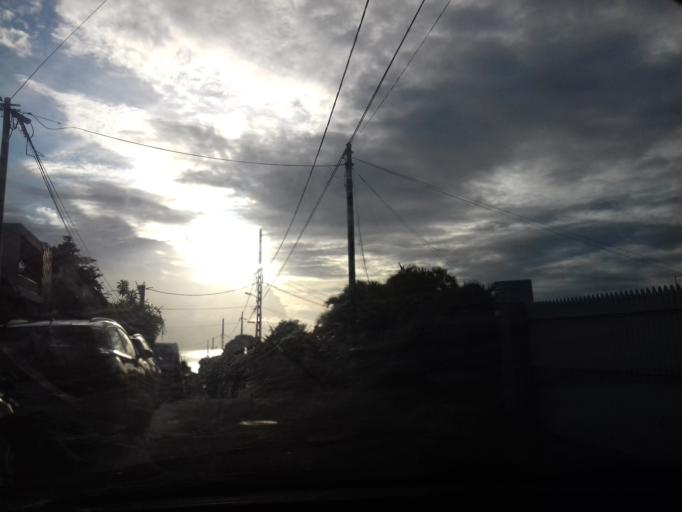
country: MQ
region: Martinique
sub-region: Martinique
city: Fort-de-France
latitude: 14.6173
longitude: -61.0885
